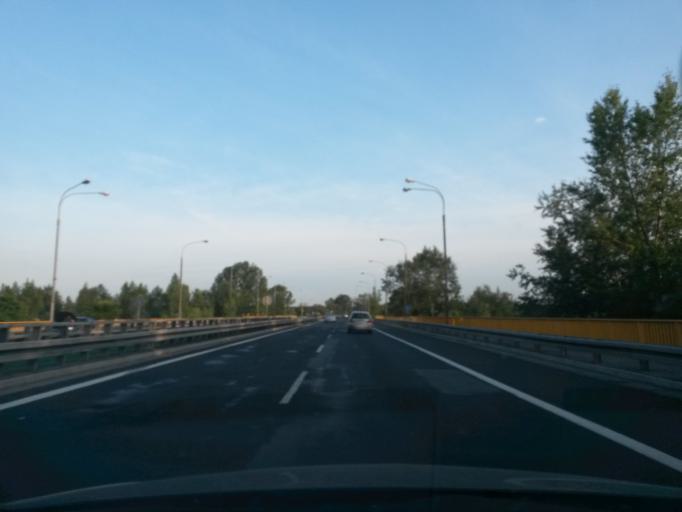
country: PL
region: Masovian Voivodeship
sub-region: Powiat nowodworski
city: Zakroczym
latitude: 52.4259
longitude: 20.6567
